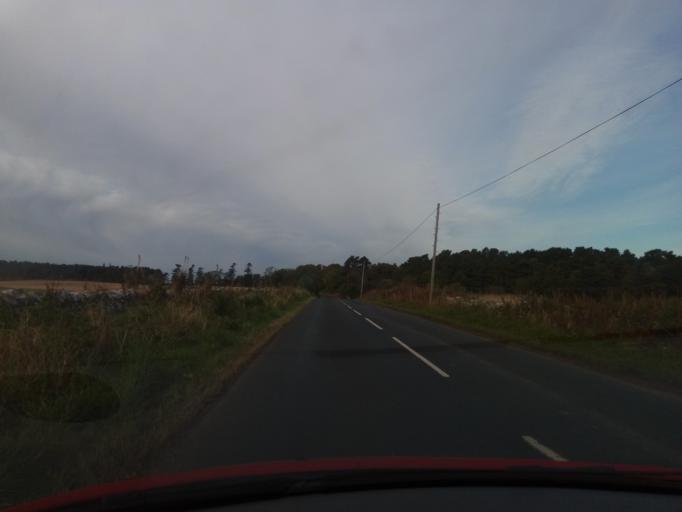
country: GB
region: Scotland
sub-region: The Scottish Borders
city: Kelso
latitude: 55.5645
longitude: -2.3456
